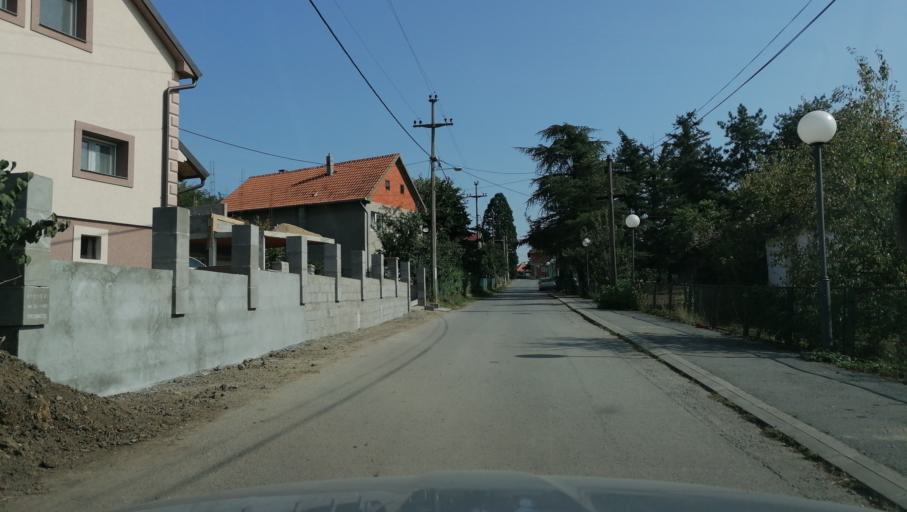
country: RS
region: Central Serbia
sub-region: Belgrade
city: Sopot
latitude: 44.5855
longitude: 20.6068
